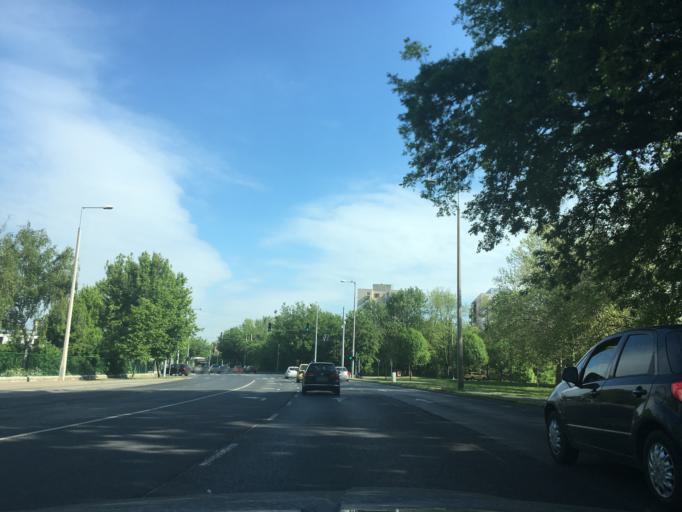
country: HU
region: Hajdu-Bihar
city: Debrecen
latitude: 47.5514
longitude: 21.6098
